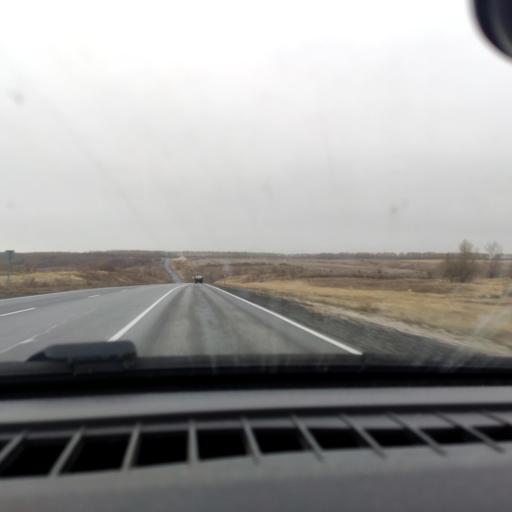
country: RU
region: Voronezj
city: Ostrogozhsk
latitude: 50.9294
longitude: 39.0572
